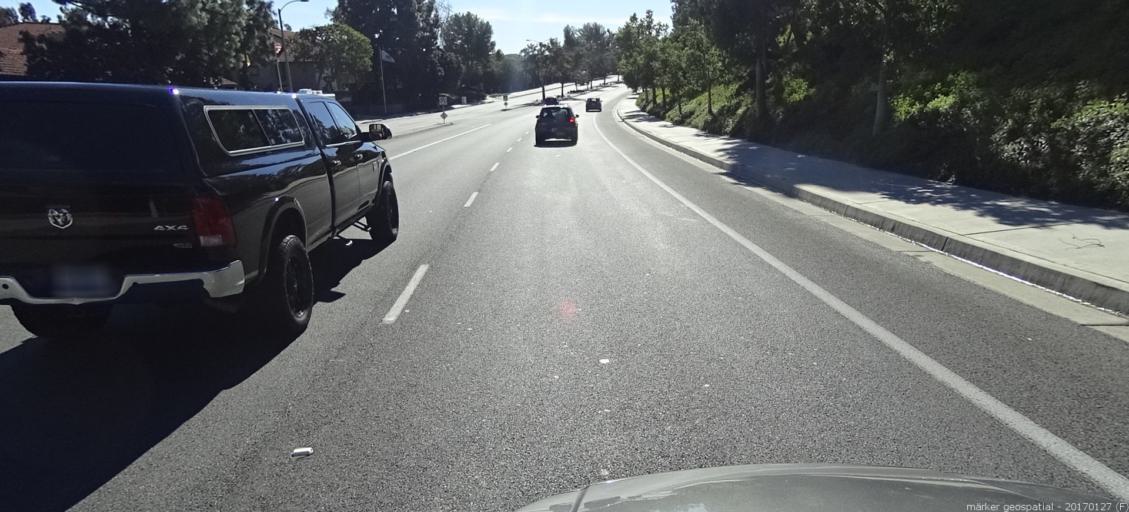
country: US
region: California
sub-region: Orange County
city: Lake Forest
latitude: 33.6516
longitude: -117.6742
